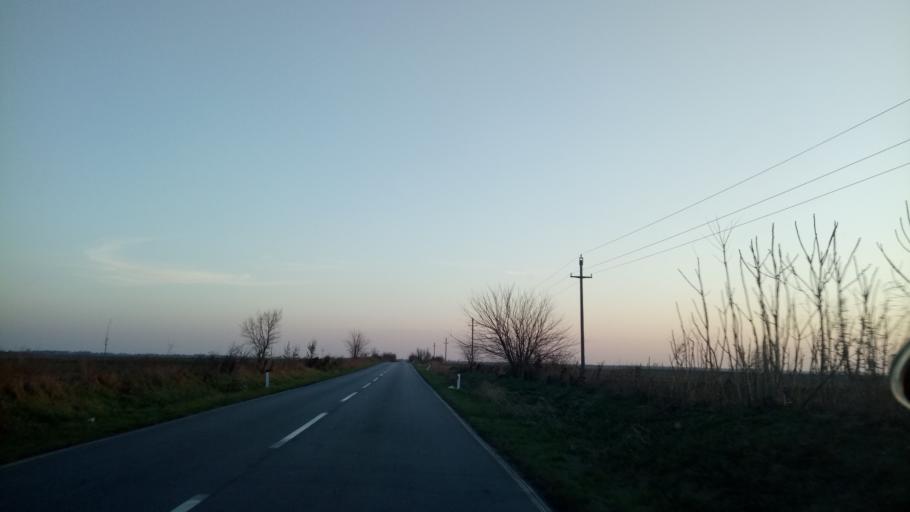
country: RS
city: Surduk
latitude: 45.0516
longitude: 20.3318
